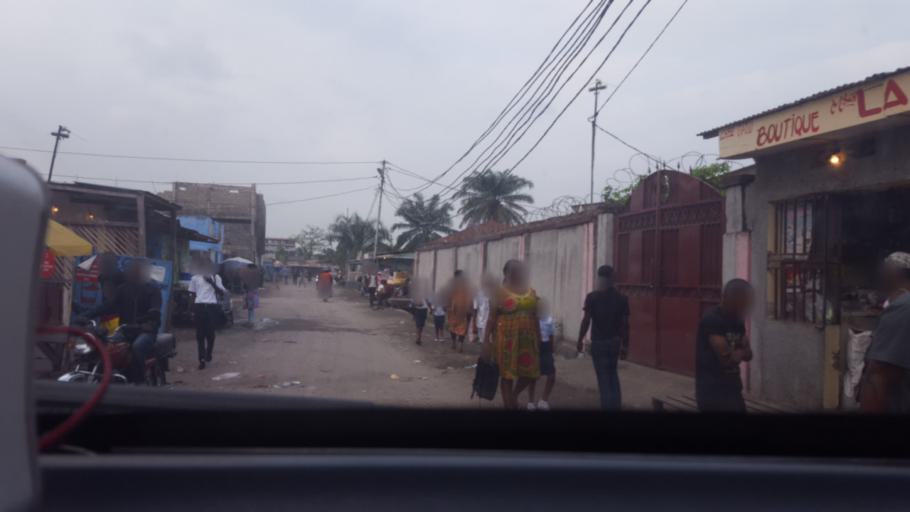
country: CD
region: Kinshasa
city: Kinshasa
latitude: -4.3338
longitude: 15.3172
